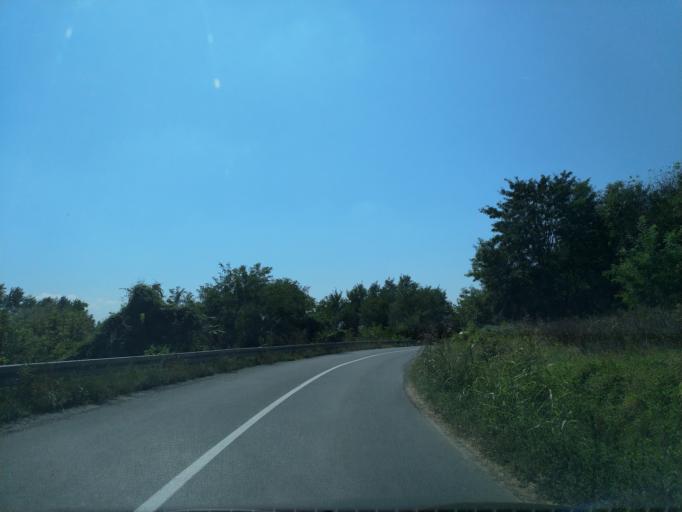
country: RS
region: Central Serbia
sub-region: Rasinski Okrug
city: Krusevac
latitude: 43.6297
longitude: 21.3718
